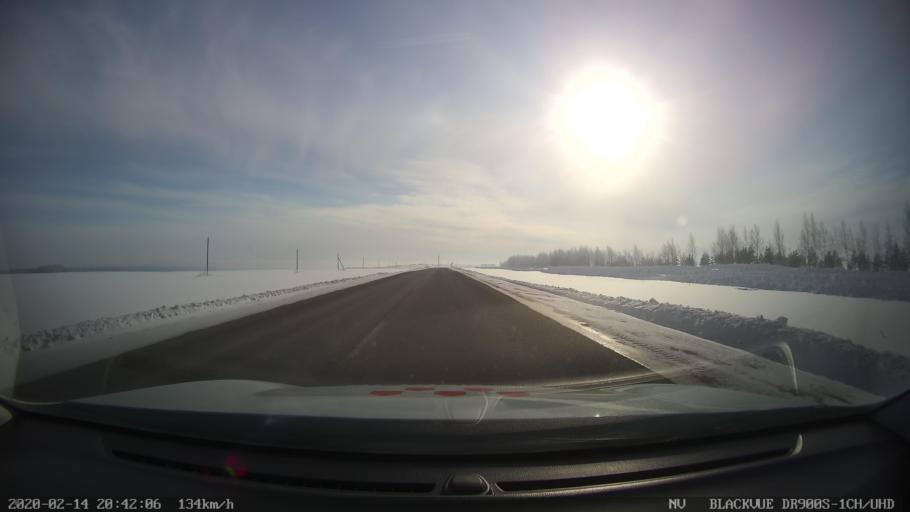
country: RU
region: Tatarstan
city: Kuybyshevskiy Zaton
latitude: 55.3210
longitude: 49.1361
